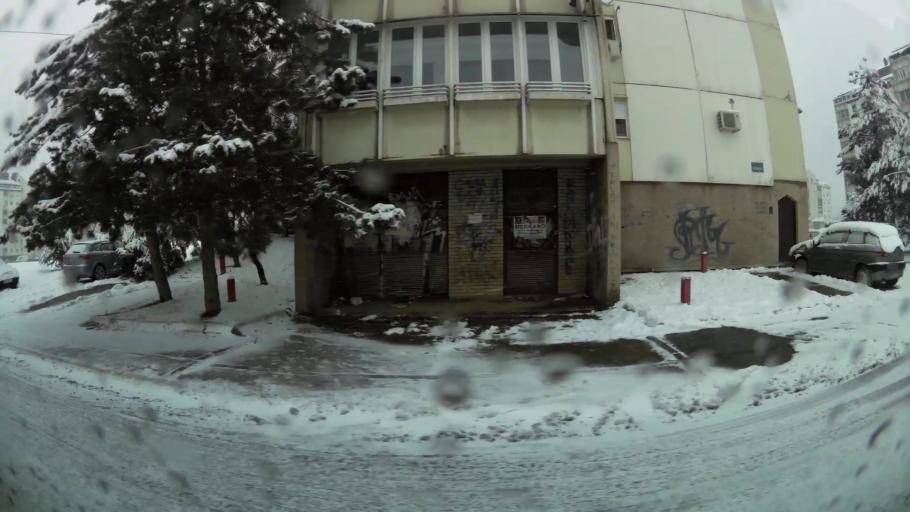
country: RS
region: Central Serbia
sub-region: Belgrade
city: Cukarica
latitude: 44.7939
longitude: 20.3712
